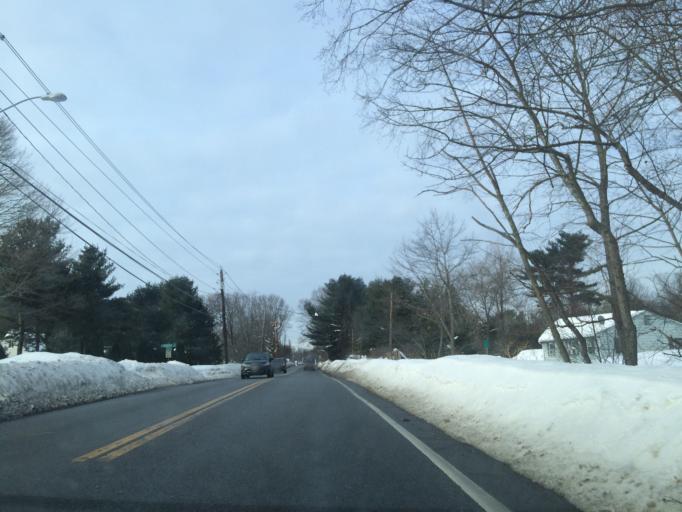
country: US
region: Massachusetts
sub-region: Middlesex County
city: Weston
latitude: 42.3630
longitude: -71.3284
